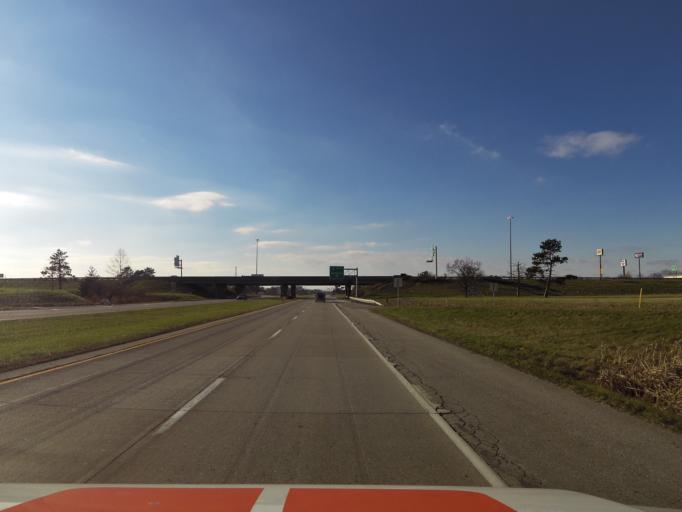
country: US
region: Indiana
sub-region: Jackson County
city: Seymour
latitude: 38.9583
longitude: -85.8415
